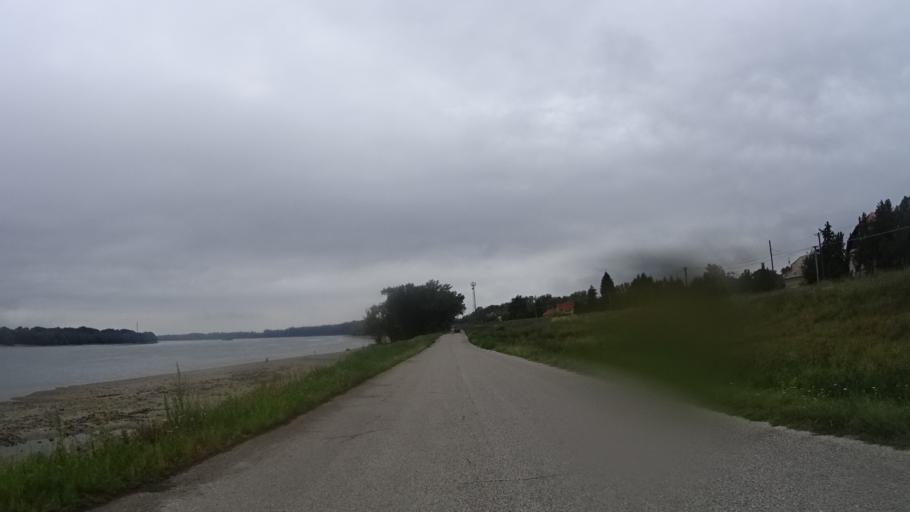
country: HU
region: Komarom-Esztergom
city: Labatlan
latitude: 47.7637
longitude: 18.4752
